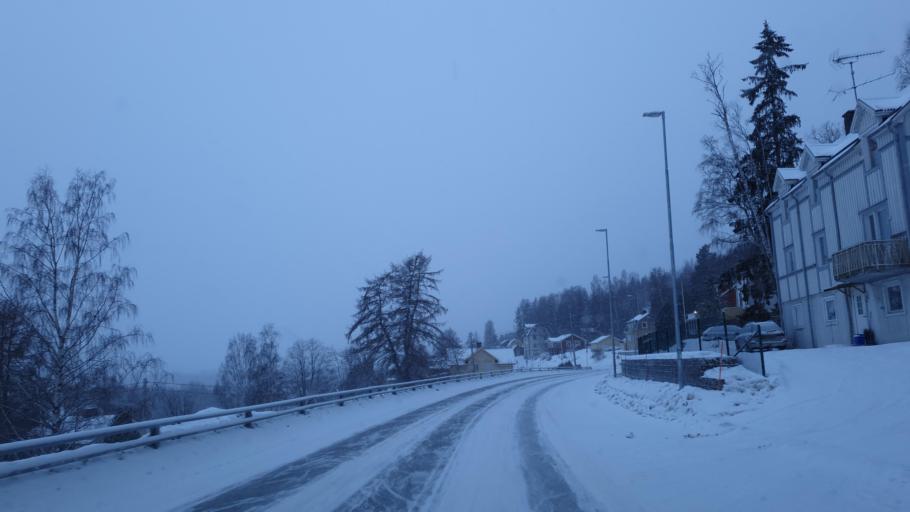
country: SE
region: Vaesternorrland
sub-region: OErnskoeldsviks Kommun
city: Ornskoldsvik
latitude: 63.2983
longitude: 18.6617
